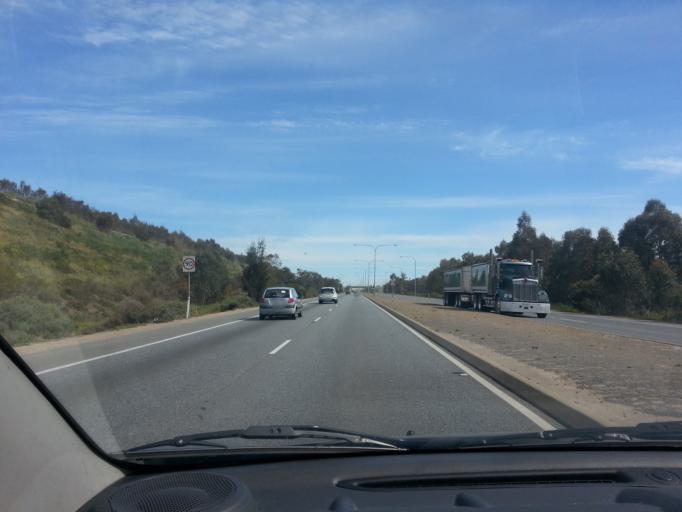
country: AU
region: South Australia
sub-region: Charles Sturt
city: Woodville North
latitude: -34.8332
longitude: 138.5552
